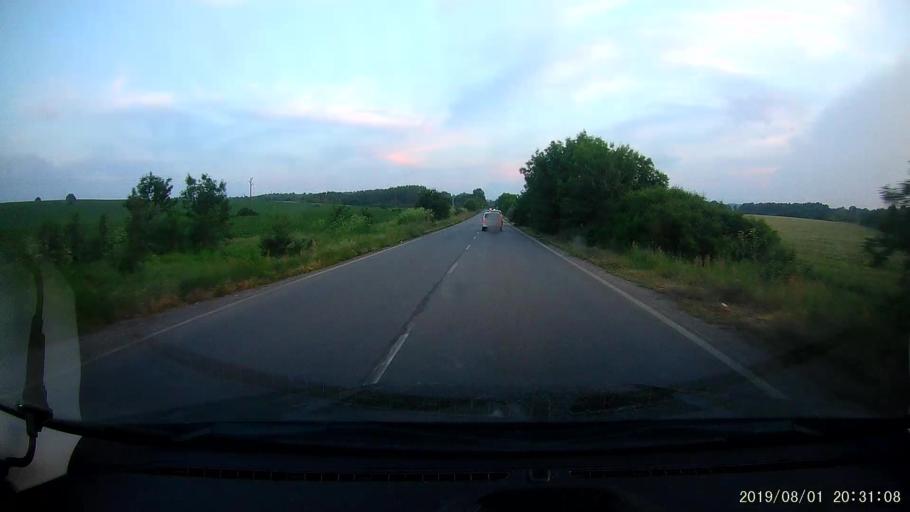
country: BG
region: Yambol
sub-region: Obshtina Elkhovo
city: Elkhovo
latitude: 42.1321
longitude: 26.5420
